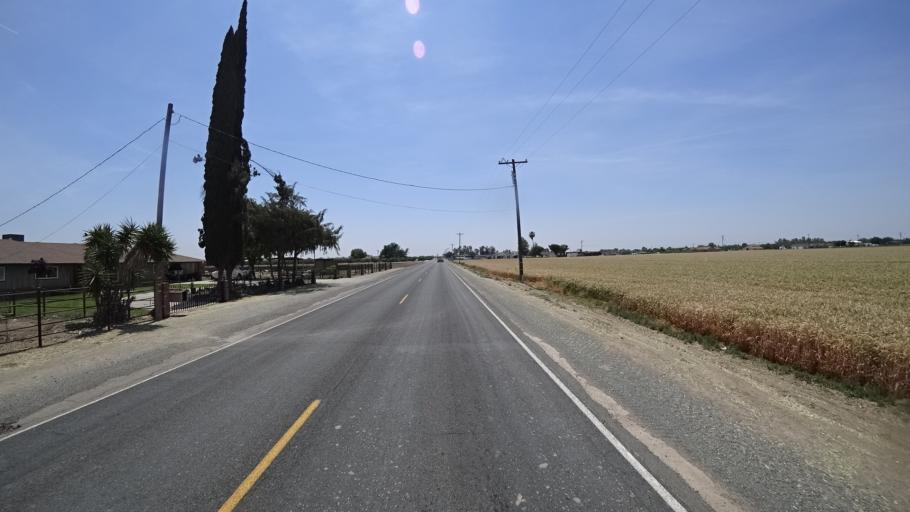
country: US
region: California
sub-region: Fresno County
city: Riverdale
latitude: 36.3968
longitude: -119.8513
